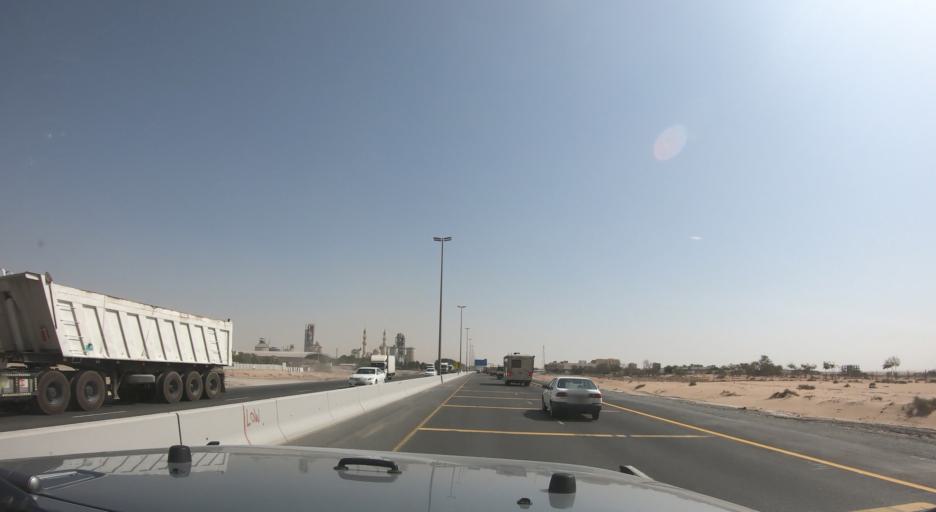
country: AE
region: Ash Shariqah
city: Sharjah
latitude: 25.2976
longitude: 55.6058
